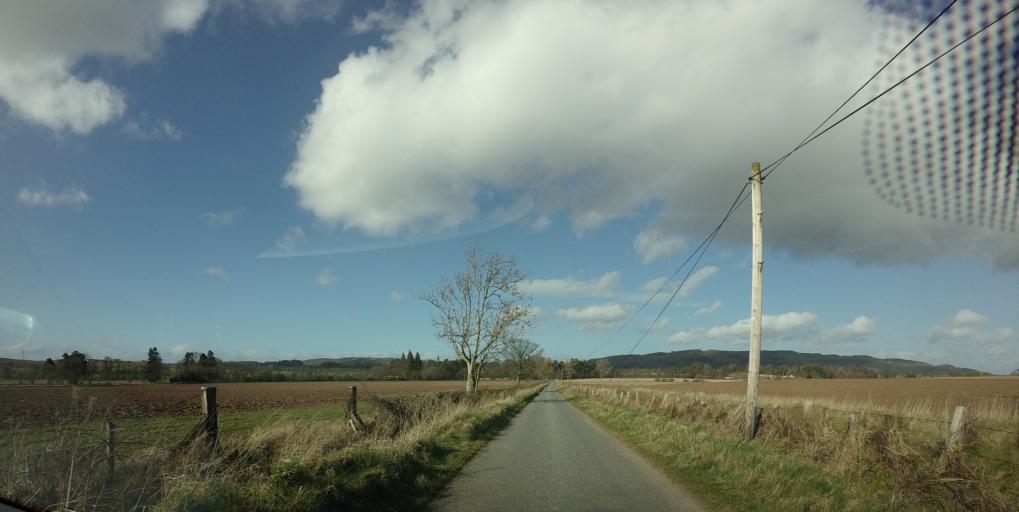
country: GB
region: Scotland
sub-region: Perth and Kinross
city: Bridge of Earn
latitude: 56.3323
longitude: -3.4296
